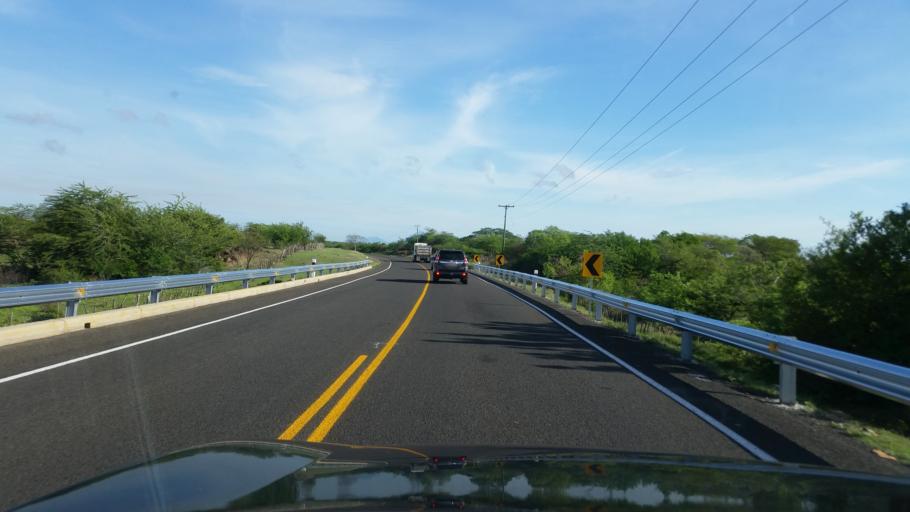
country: NI
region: Leon
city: La Paz Centro
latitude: 12.2571
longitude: -86.7255
